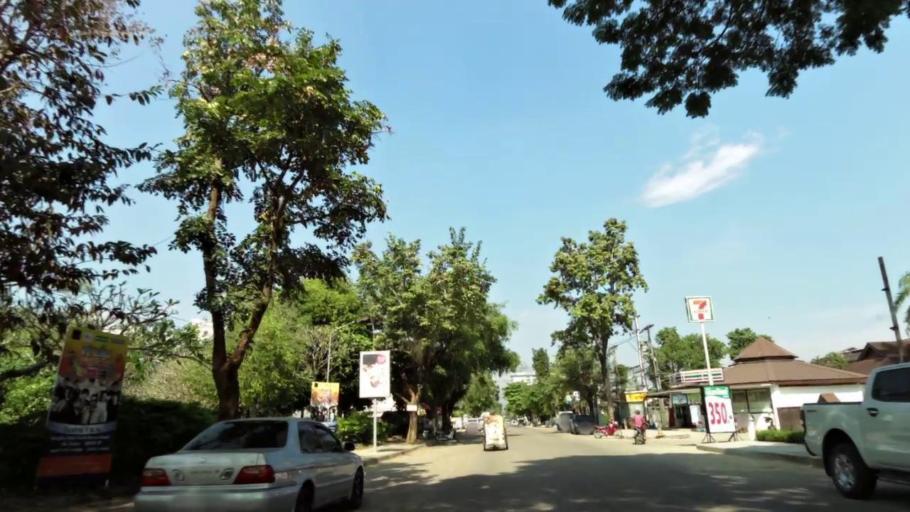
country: TH
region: Chiang Rai
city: Chiang Rai
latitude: 19.8938
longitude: 99.8274
